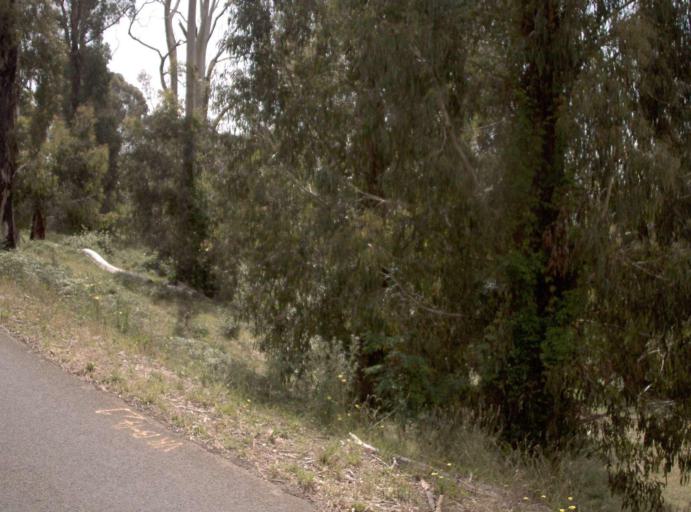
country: AU
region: Victoria
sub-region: Latrobe
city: Traralgon
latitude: -38.3311
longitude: 146.5726
